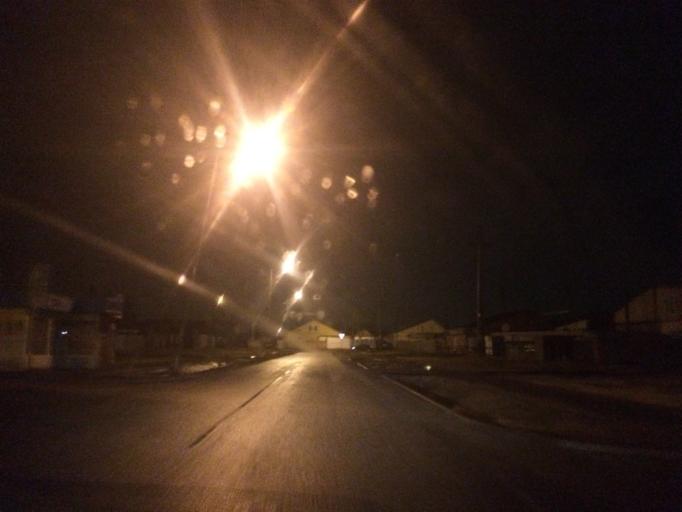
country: KZ
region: Astana Qalasy
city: Astana
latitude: 51.1947
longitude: 71.3834
